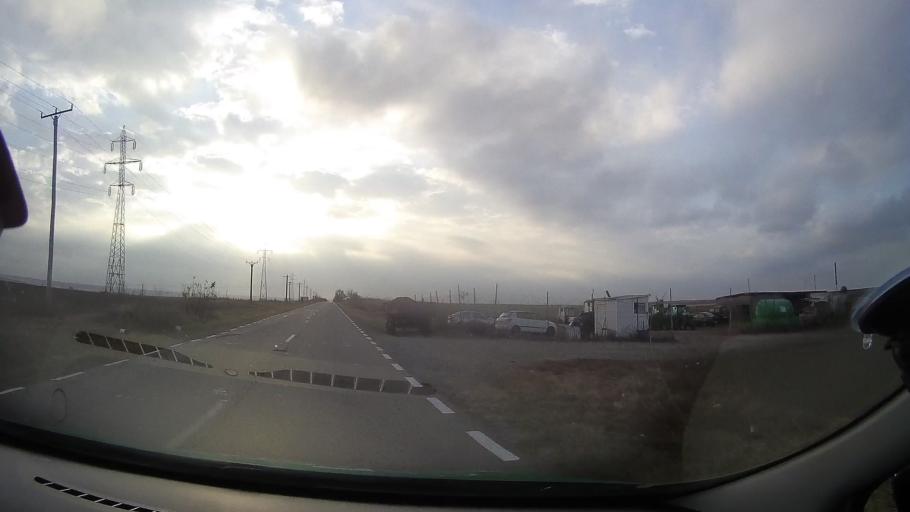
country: RO
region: Constanta
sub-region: Comuna Pestera
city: Pestera
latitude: 44.2151
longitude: 28.1870
